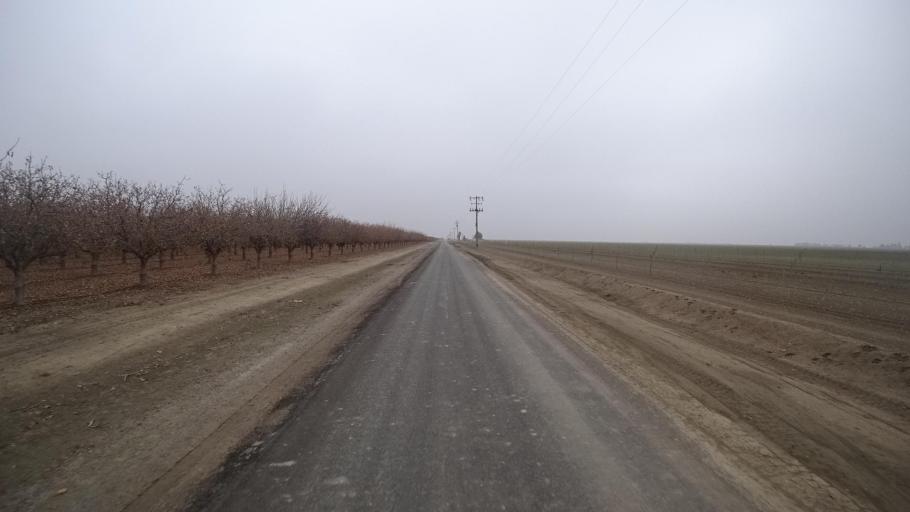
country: US
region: California
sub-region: Kern County
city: Wasco
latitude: 35.7010
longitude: -119.4906
